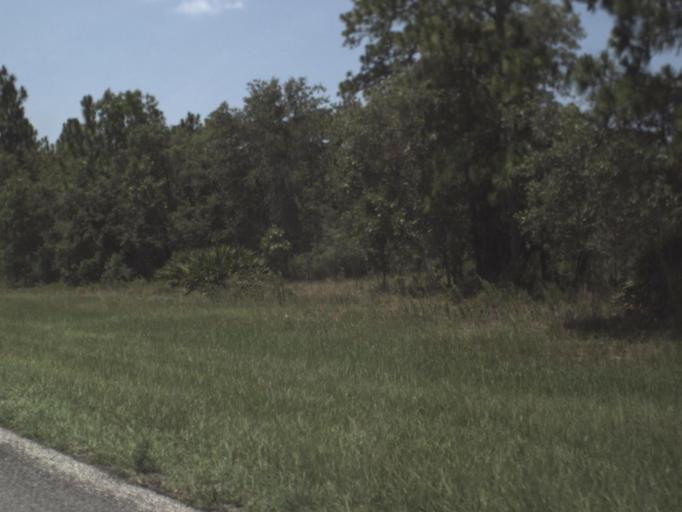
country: US
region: Florida
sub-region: Citrus County
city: Sugarmill Woods
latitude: 28.6704
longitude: -82.5525
